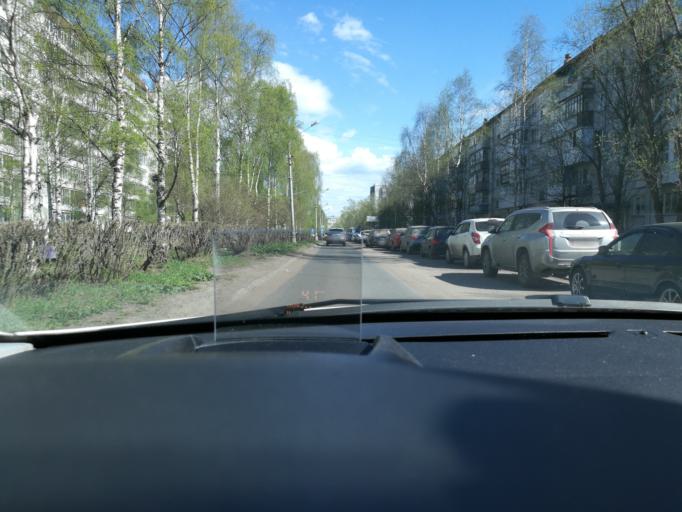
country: RU
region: Arkhangelskaya
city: Arkhangel'sk
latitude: 64.5481
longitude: 40.5309
